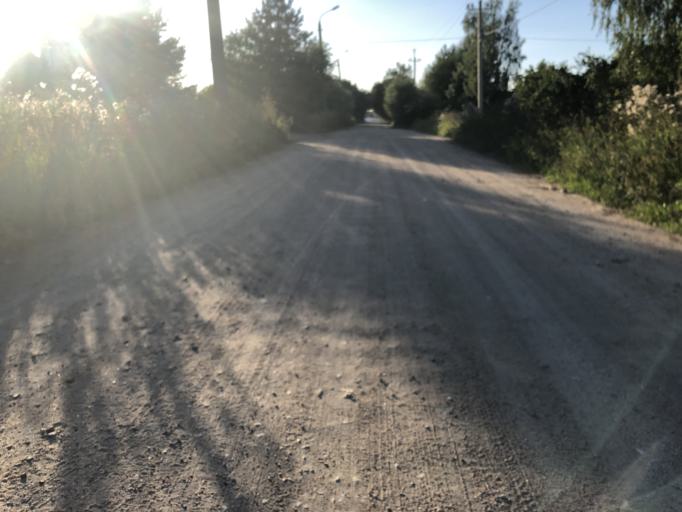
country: RU
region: Tverskaya
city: Rzhev
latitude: 56.2445
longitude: 34.3050
